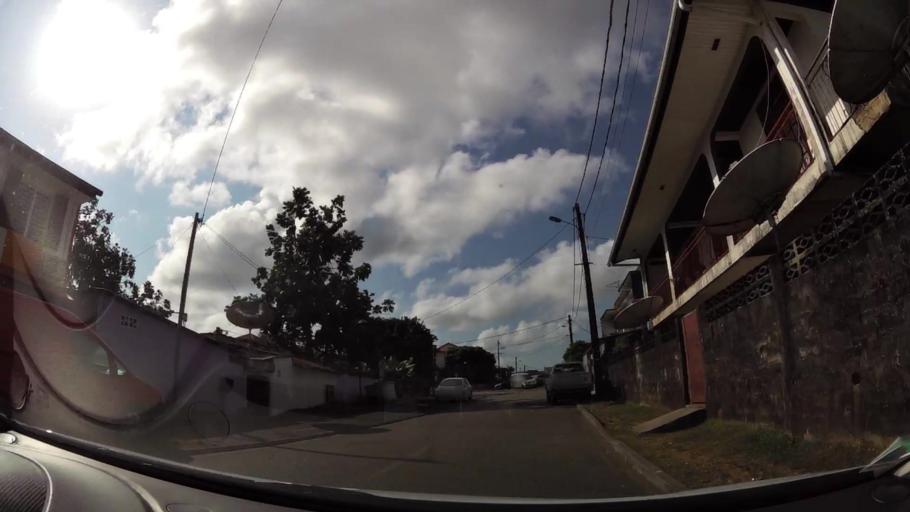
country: GF
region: Guyane
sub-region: Guyane
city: Cayenne
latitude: 4.9283
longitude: -52.3222
